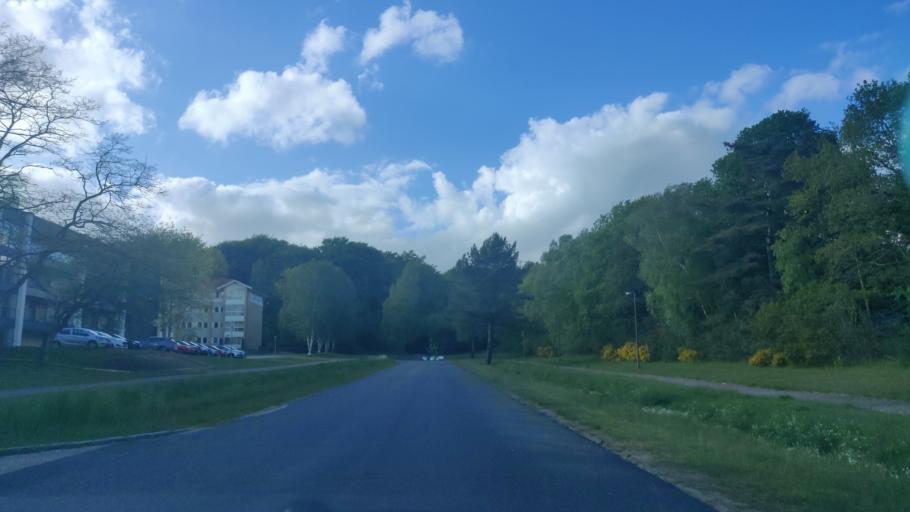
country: DK
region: Central Jutland
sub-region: Viborg Kommune
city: Bjerringbro
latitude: 56.3791
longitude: 9.6443
